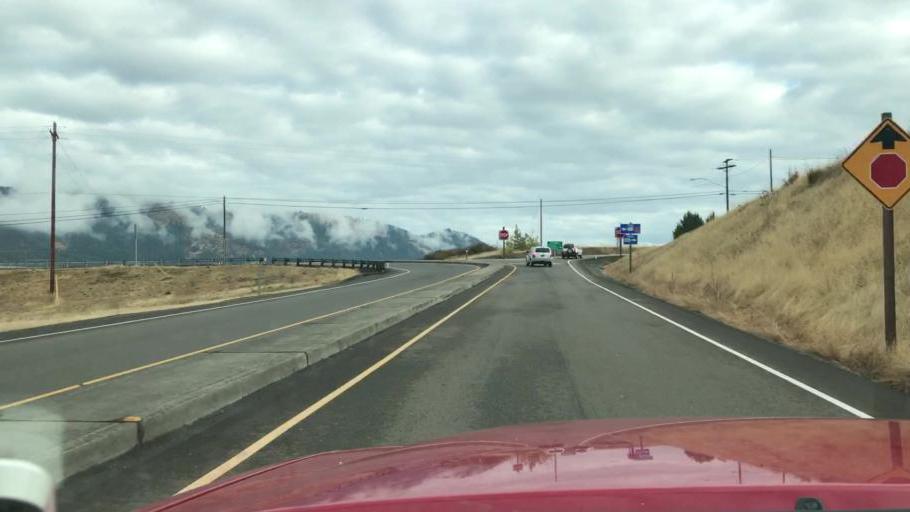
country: US
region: Oregon
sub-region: Douglas County
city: Tri-City
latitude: 42.9725
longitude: -123.3355
